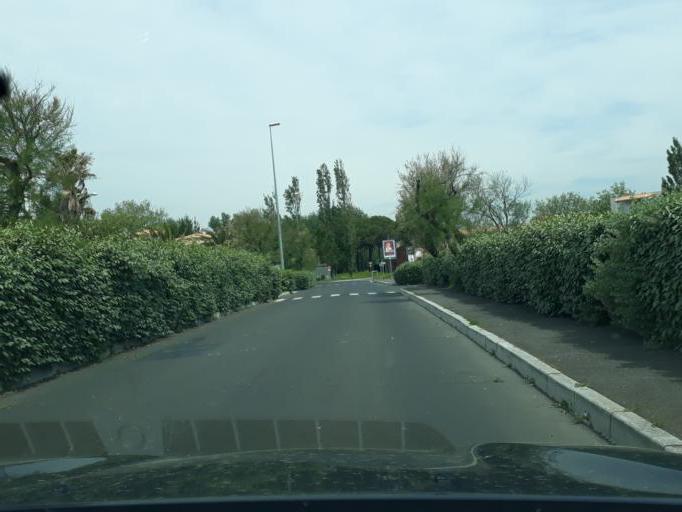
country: FR
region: Languedoc-Roussillon
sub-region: Departement de l'Herault
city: Le Cap d'Agde
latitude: 43.2768
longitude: 3.4882
